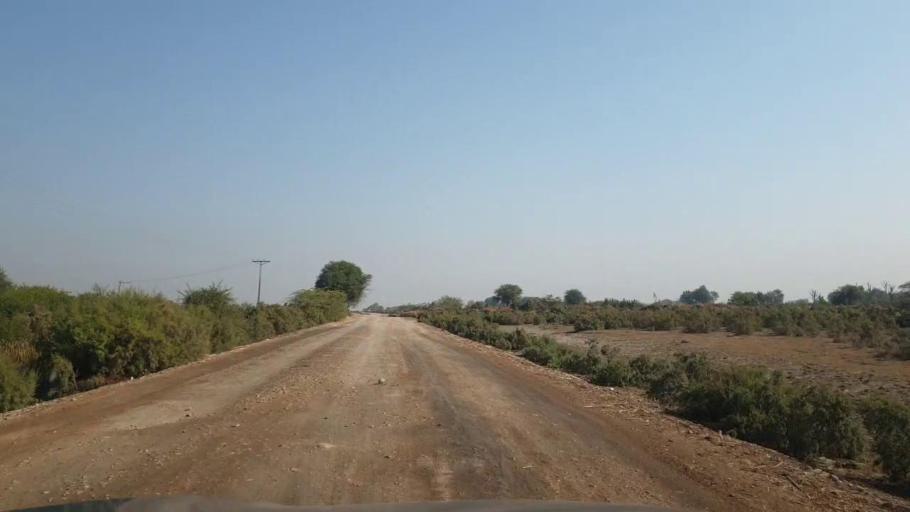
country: PK
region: Sindh
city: Berani
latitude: 25.6309
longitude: 68.8624
